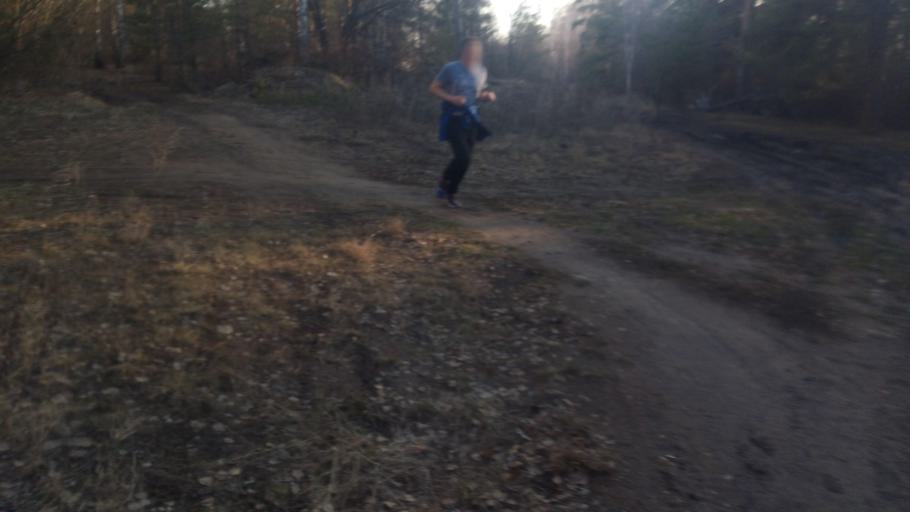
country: RU
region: Chelyabinsk
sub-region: Gorod Chelyabinsk
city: Chelyabinsk
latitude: 55.1383
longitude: 61.3290
